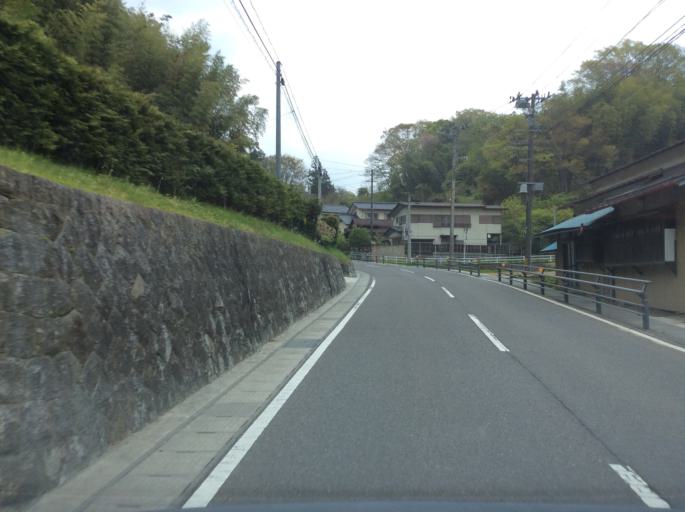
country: JP
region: Fukushima
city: Miharu
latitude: 37.4453
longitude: 140.4954
